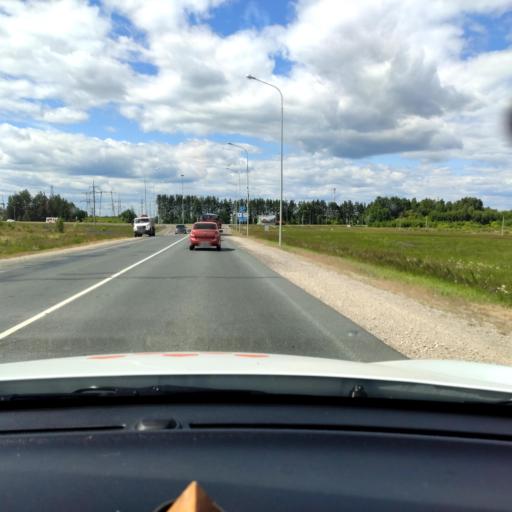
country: RU
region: Mariy-El
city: Volzhsk
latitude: 55.9109
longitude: 48.3700
